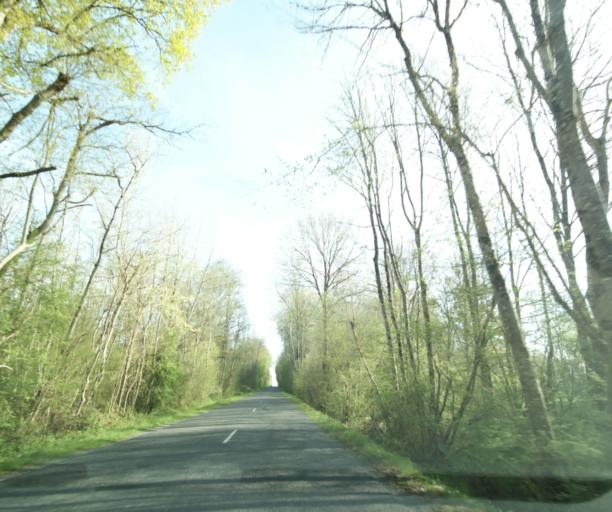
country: FR
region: Ile-de-France
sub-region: Departement de Seine-et-Marne
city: Nangis
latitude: 48.5333
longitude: 2.9830
